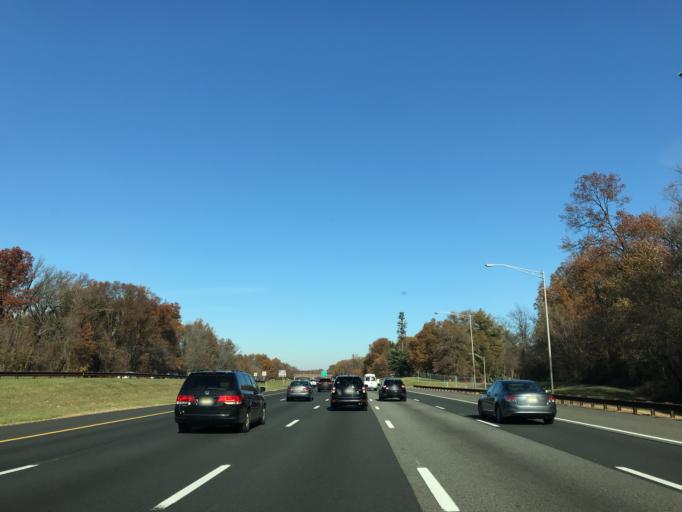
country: US
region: New Jersey
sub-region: Middlesex County
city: Iselin
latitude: 40.6075
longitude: -74.3131
